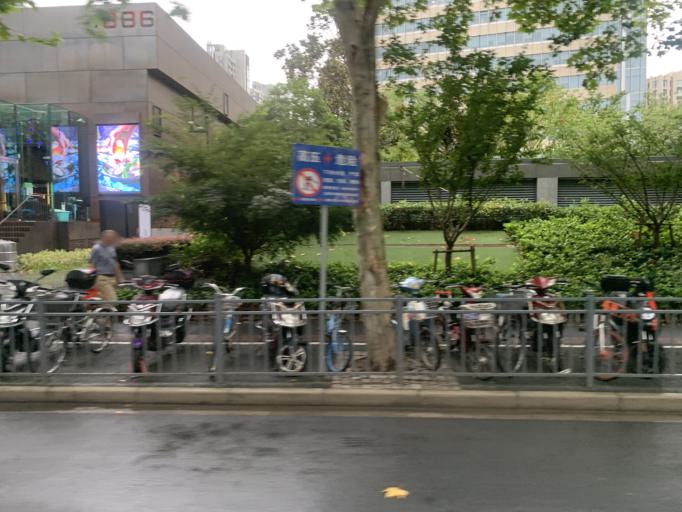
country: CN
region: Shanghai Shi
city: Luwan
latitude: 31.2133
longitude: 121.4734
